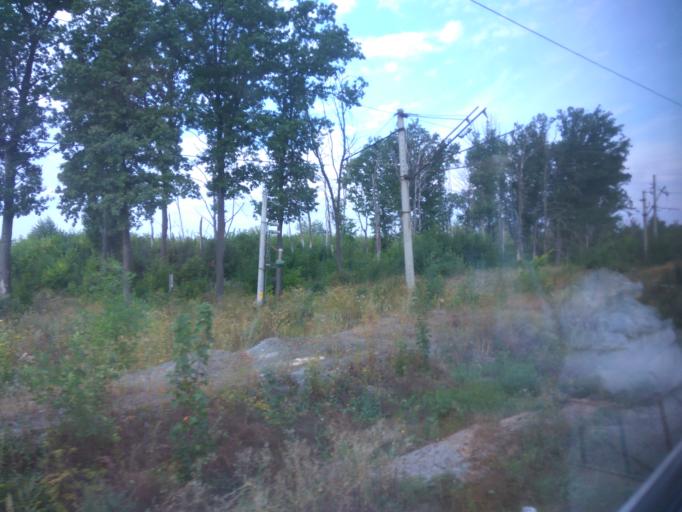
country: RU
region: Saratov
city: Rtishchevo
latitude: 52.2222
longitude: 43.8629
